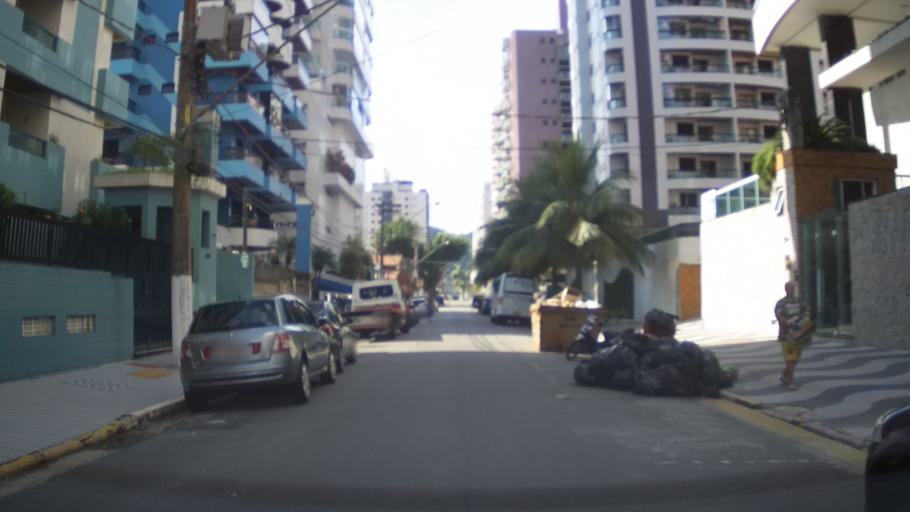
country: BR
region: Sao Paulo
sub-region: Praia Grande
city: Praia Grande
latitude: -24.0134
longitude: -46.4028
